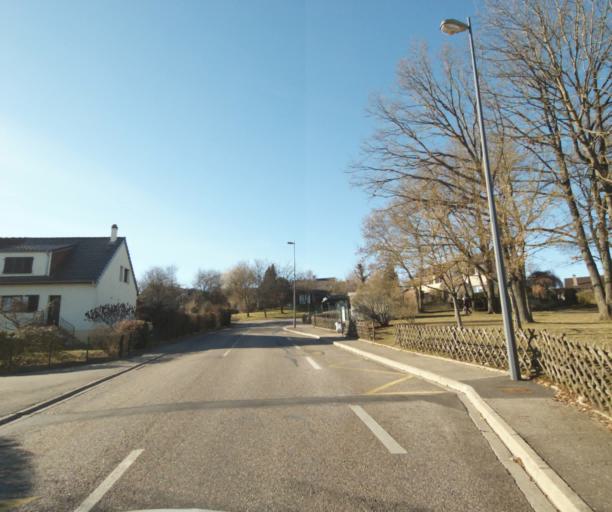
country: FR
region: Lorraine
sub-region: Departement de Meurthe-et-Moselle
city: Vandoeuvre-les-Nancy
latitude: 48.6413
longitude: 6.1979
